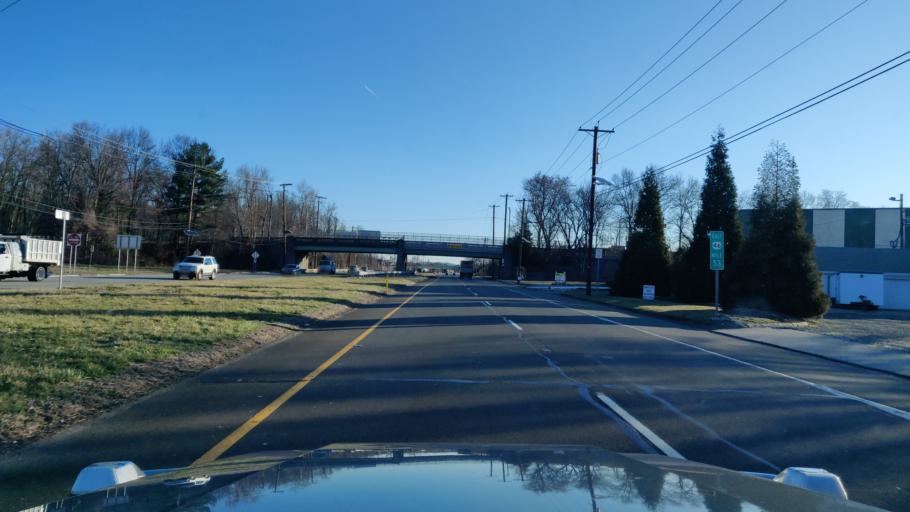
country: US
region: New Jersey
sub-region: Essex County
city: Fairfield
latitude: 40.8727
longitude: -74.3038
